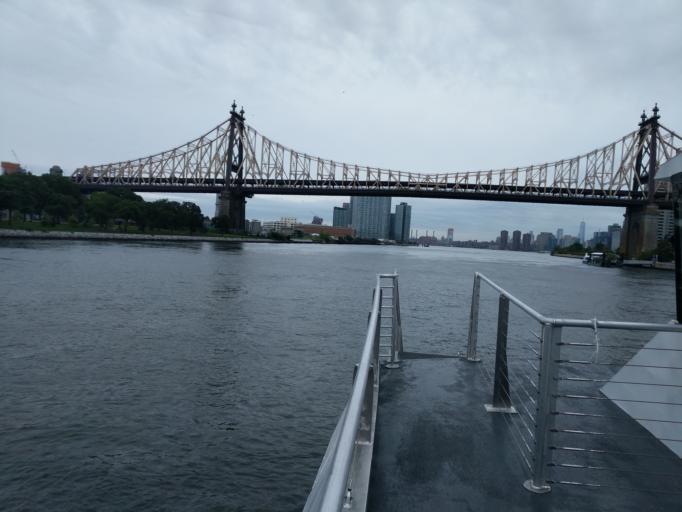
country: US
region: New York
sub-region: Queens County
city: Long Island City
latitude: 40.7587
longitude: -73.9496
